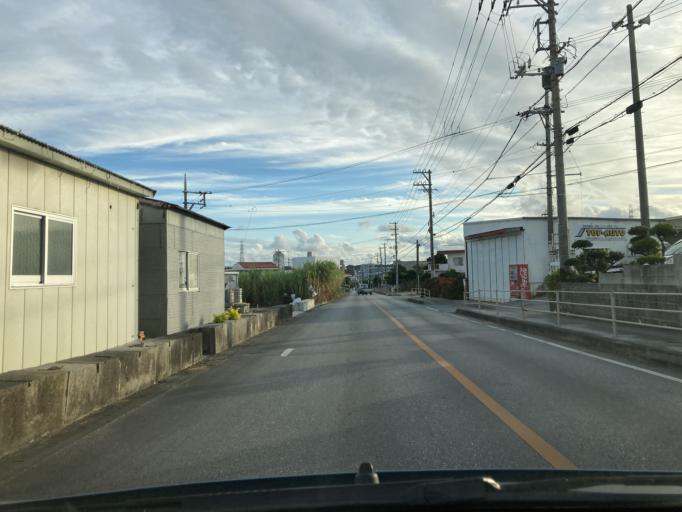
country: JP
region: Okinawa
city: Itoman
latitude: 26.1420
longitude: 127.6888
